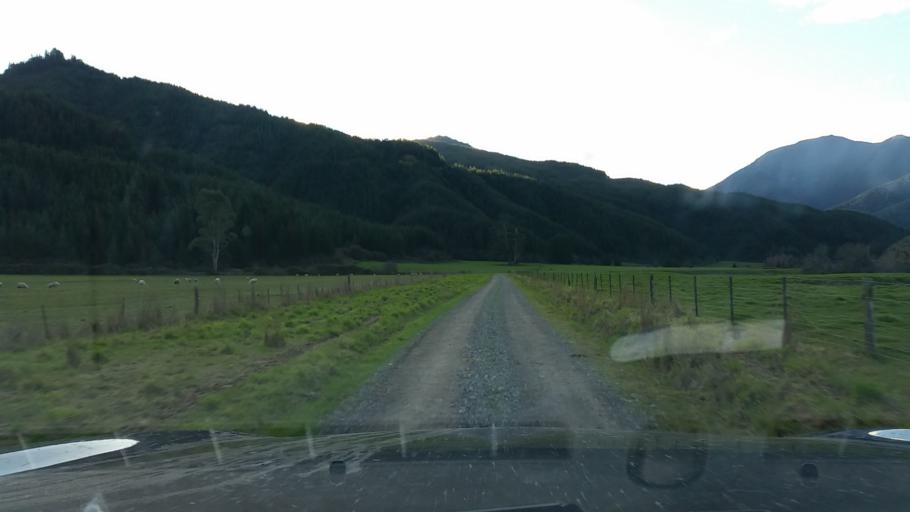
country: NZ
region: Nelson
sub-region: Nelson City
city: Nelson
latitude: -41.5355
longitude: 173.4895
